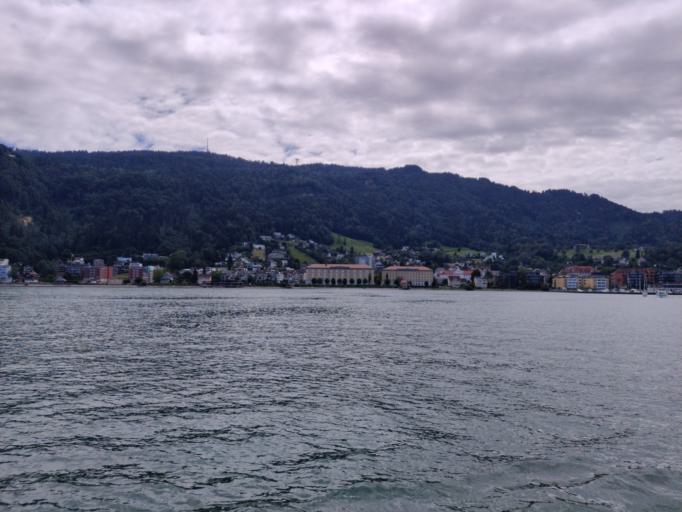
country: AT
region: Vorarlberg
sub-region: Politischer Bezirk Bregenz
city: Bregenz
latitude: 47.5108
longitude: 9.7447
